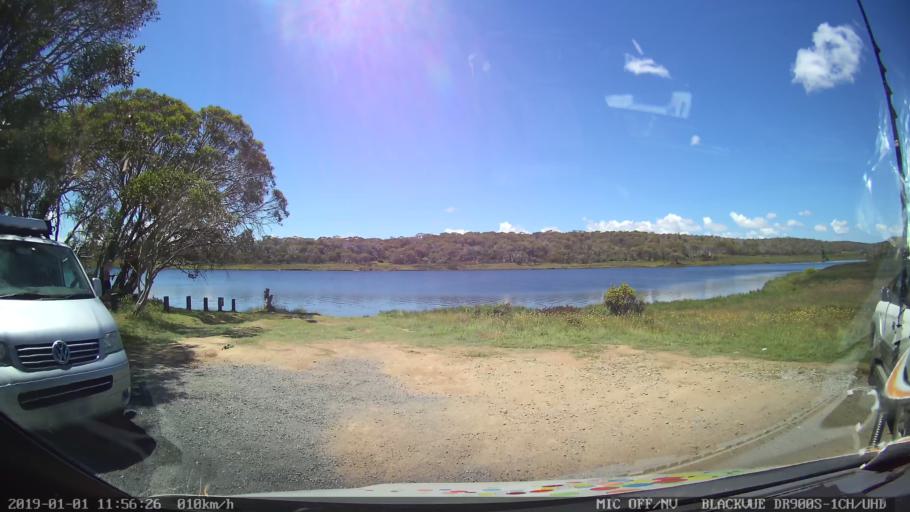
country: AU
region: New South Wales
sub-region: Snowy River
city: Jindabyne
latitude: -35.8863
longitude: 148.4508
